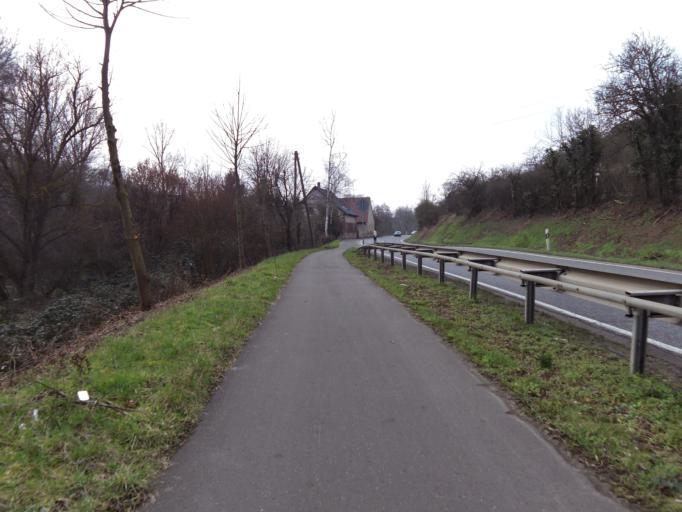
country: DE
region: Rheinland-Pfalz
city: Mertesheim
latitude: 49.5722
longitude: 8.1415
